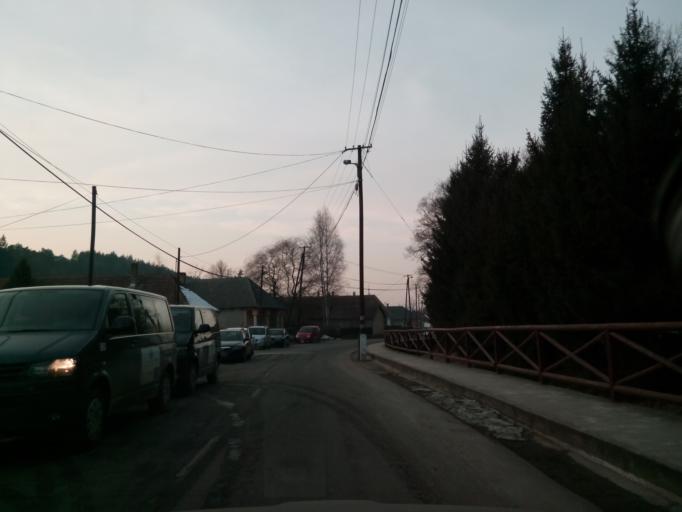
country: HU
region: Borsod-Abauj-Zemplen
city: Gonc
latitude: 48.4833
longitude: 21.3557
